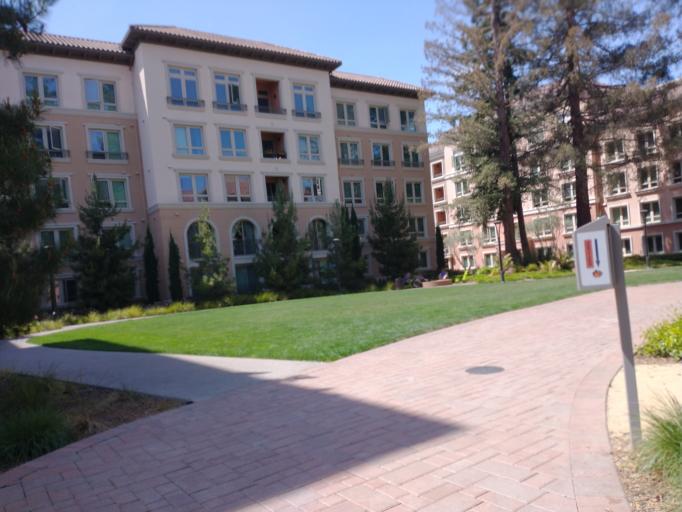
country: US
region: California
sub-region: Santa Clara County
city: Santa Clara
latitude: 37.3808
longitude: -121.9715
